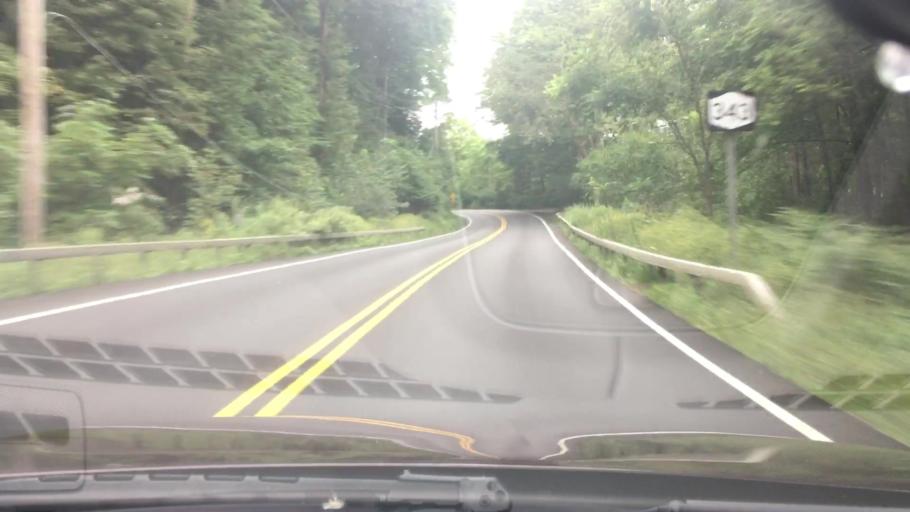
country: US
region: New York
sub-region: Dutchess County
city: Dover Plains
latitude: 41.8573
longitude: -73.5199
